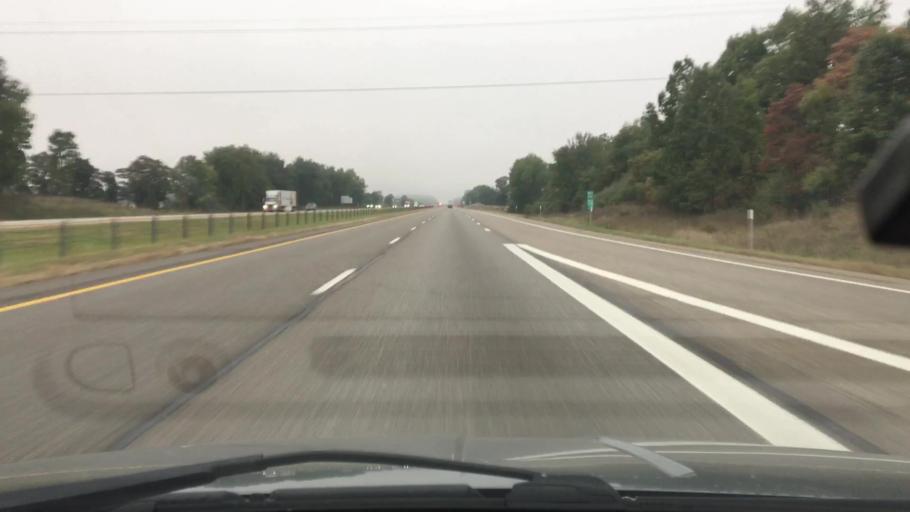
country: US
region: Michigan
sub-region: Calhoun County
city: Albion
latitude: 42.2839
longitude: -84.8036
